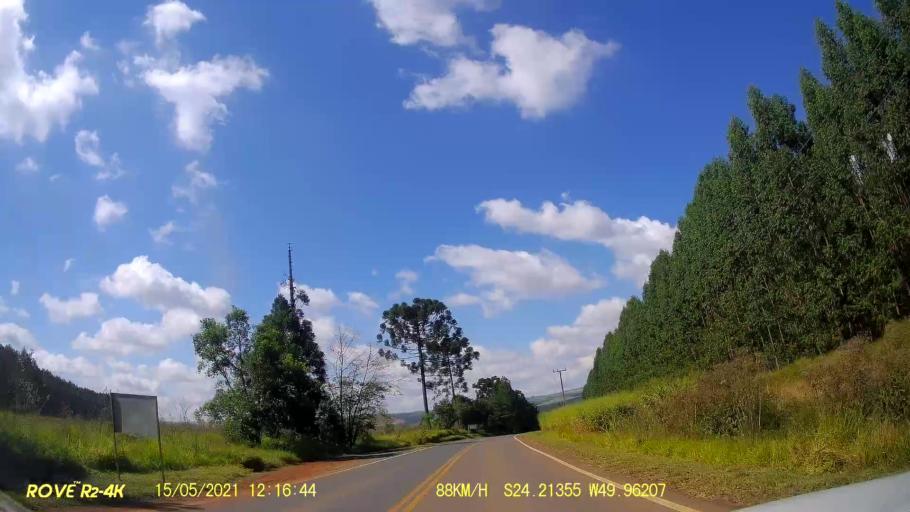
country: BR
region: Parana
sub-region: Jaguariaiva
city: Jaguariaiva
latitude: -24.2135
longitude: -49.9621
